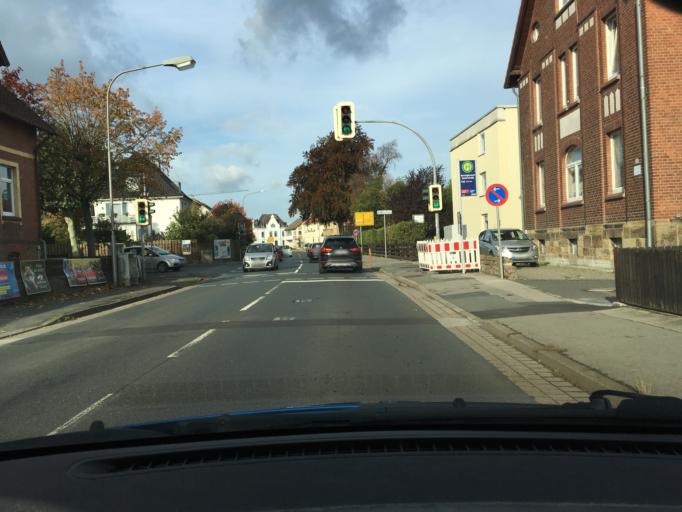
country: DE
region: Lower Saxony
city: Barsinghausen
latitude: 52.3049
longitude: 9.4629
